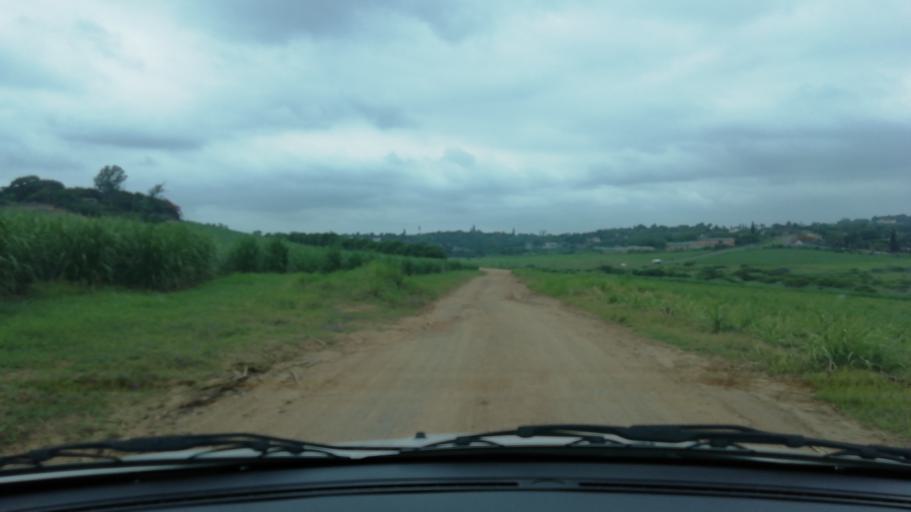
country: ZA
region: KwaZulu-Natal
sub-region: uThungulu District Municipality
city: Empangeni
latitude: -28.7347
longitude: 31.9079
